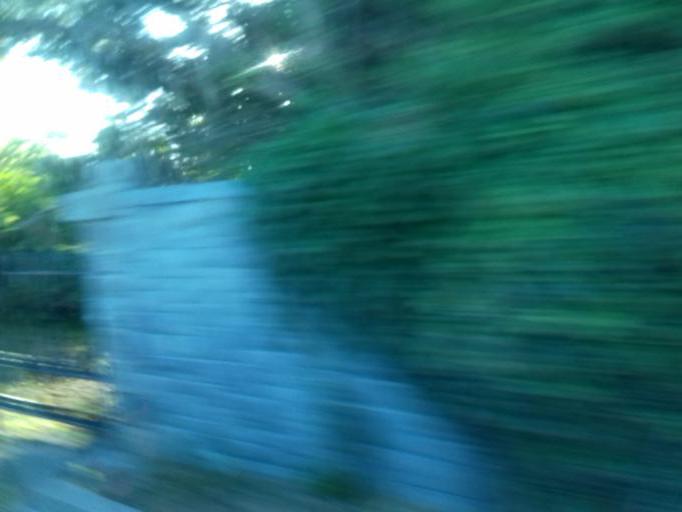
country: IE
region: Leinster
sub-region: Fingal County
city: Blanchardstown
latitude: 53.4433
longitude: -6.3458
